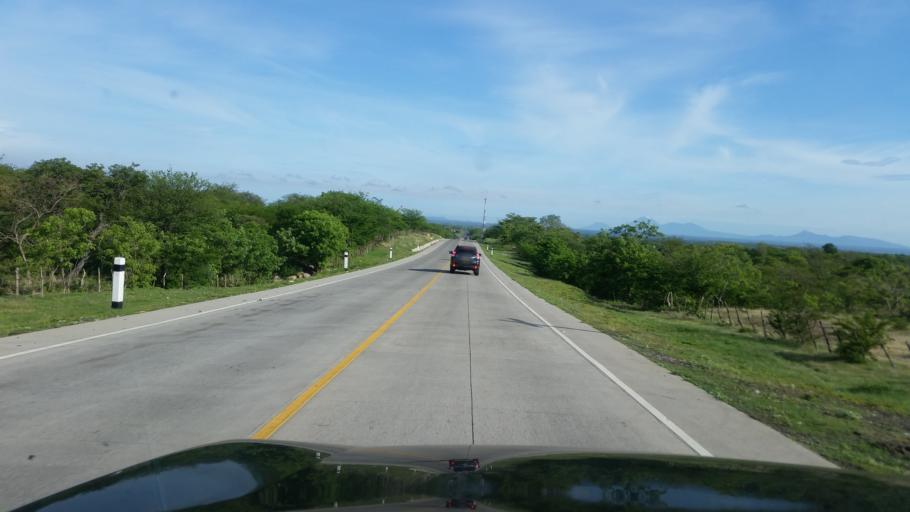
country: NI
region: Leon
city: La Paz Centro
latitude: 12.2113
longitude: -86.6827
